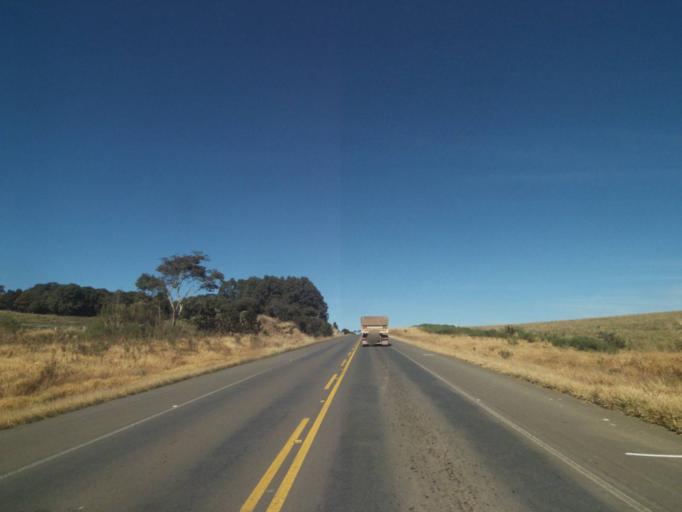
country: BR
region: Parana
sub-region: Tibagi
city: Tibagi
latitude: -24.7600
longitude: -50.4700
